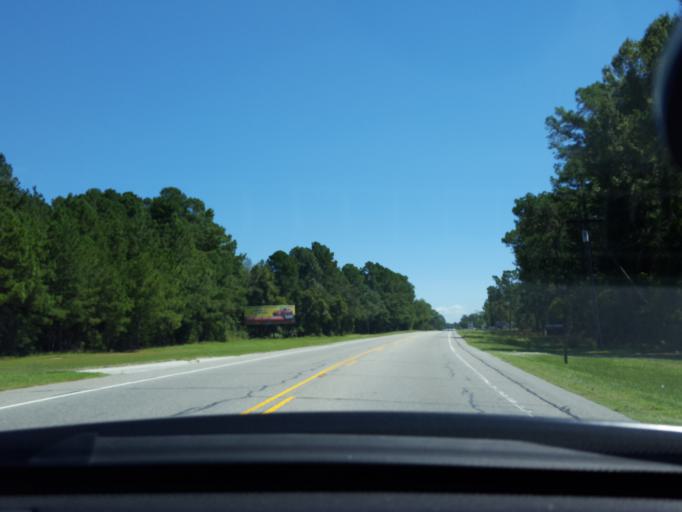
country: US
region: North Carolina
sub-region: Bladen County
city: Elizabethtown
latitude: 34.6467
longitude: -78.5857
